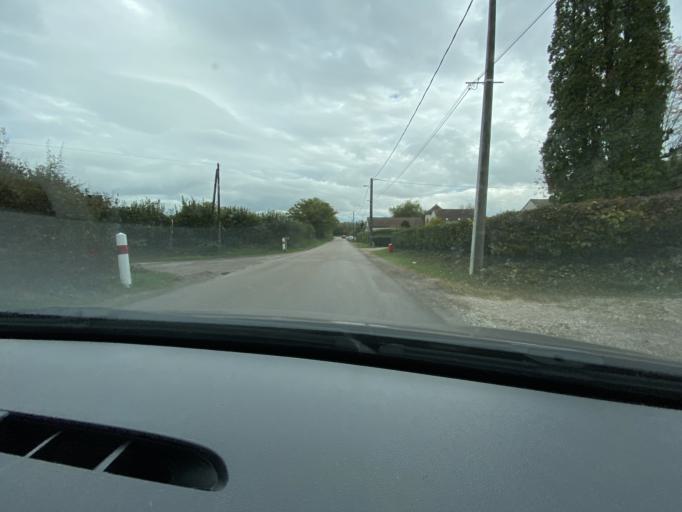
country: FR
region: Bourgogne
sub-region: Departement de la Cote-d'Or
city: Saulieu
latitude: 47.2765
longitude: 4.2143
